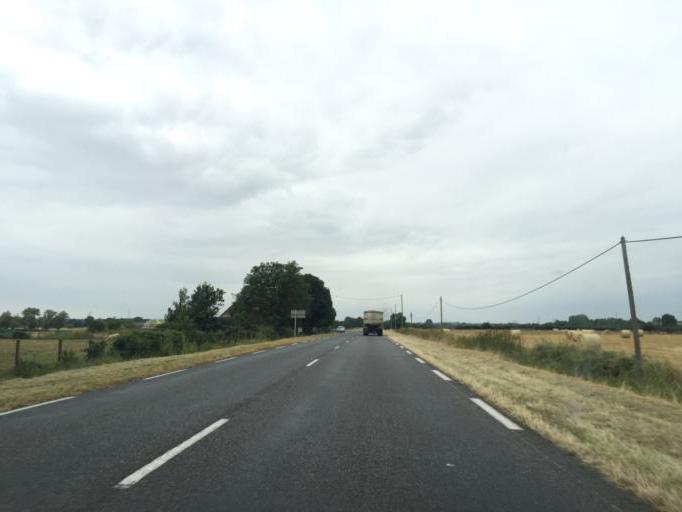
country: FR
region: Auvergne
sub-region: Departement de l'Allier
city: Saint-Pourcain-sur-Sioule
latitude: 46.2596
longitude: 3.2883
